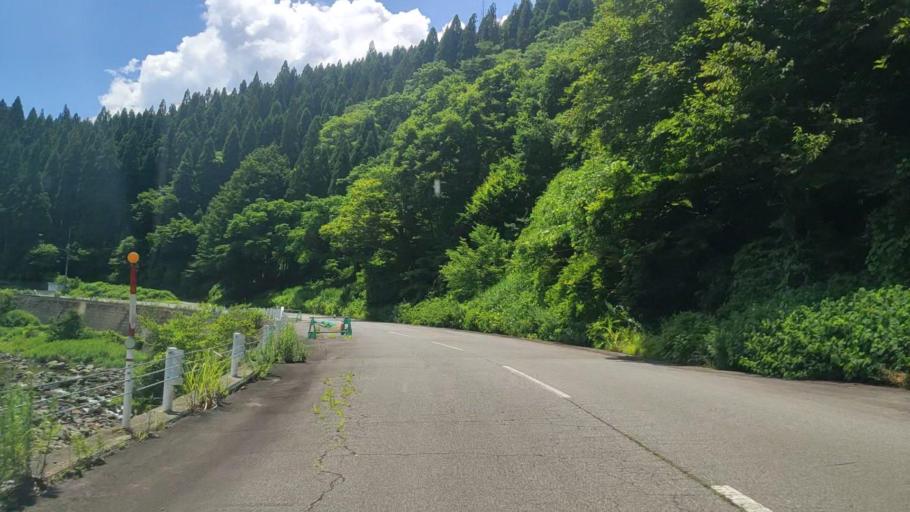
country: JP
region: Fukui
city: Ono
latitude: 35.8550
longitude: 136.4640
